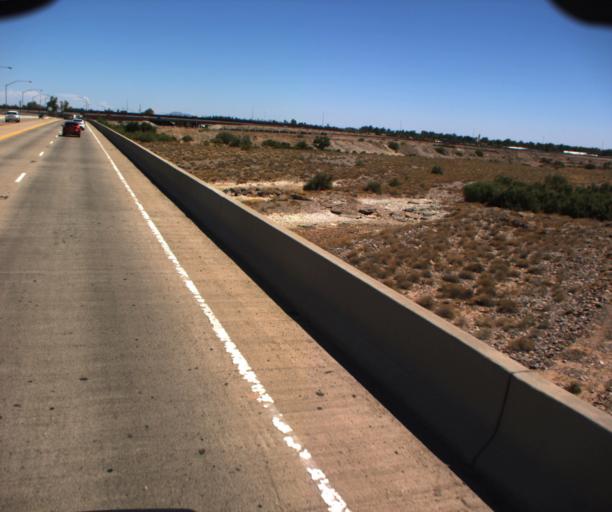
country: US
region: Arizona
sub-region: Maricopa County
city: Mesa
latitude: 33.4613
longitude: -111.8423
